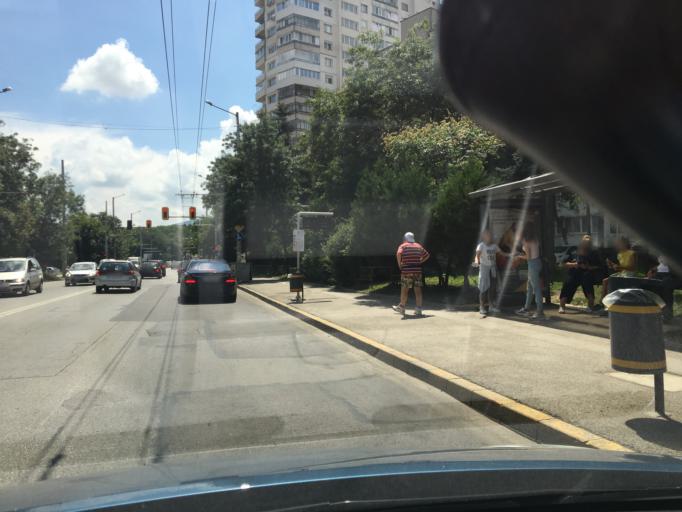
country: BG
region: Sofia-Capital
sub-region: Stolichna Obshtina
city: Sofia
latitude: 42.6755
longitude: 23.3035
